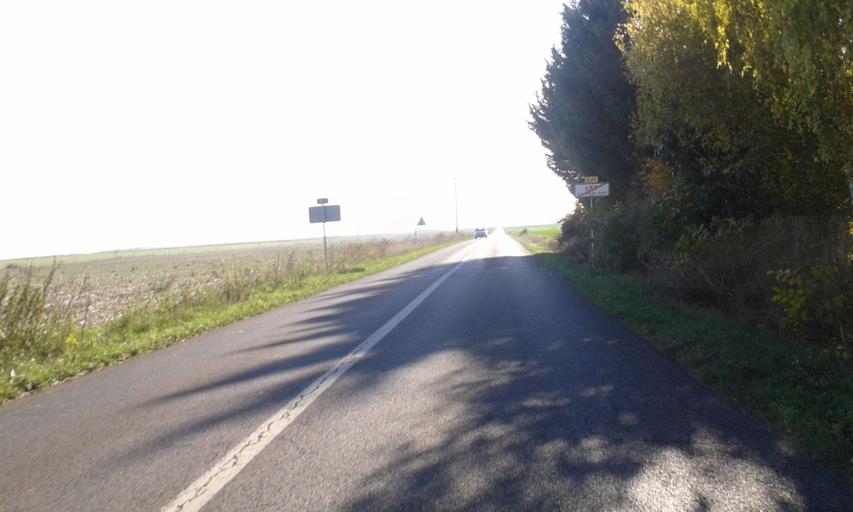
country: FR
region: Centre
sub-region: Departement du Loir-et-Cher
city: Mer
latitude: 47.7793
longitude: 1.5122
